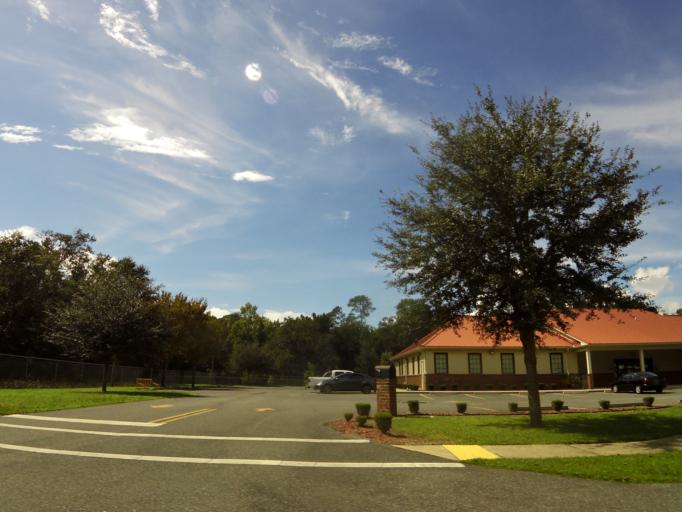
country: US
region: Florida
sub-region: Union County
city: Lake Butler
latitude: 30.0210
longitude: -82.3323
